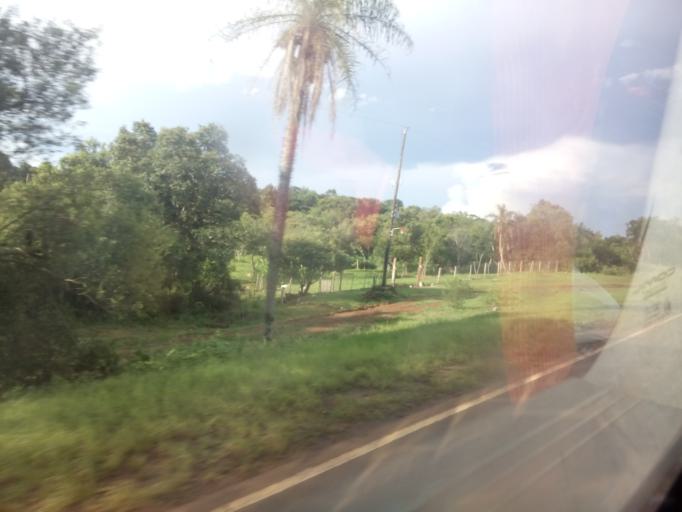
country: AR
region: Misiones
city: Santa Ana
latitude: -27.3868
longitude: -55.5923
